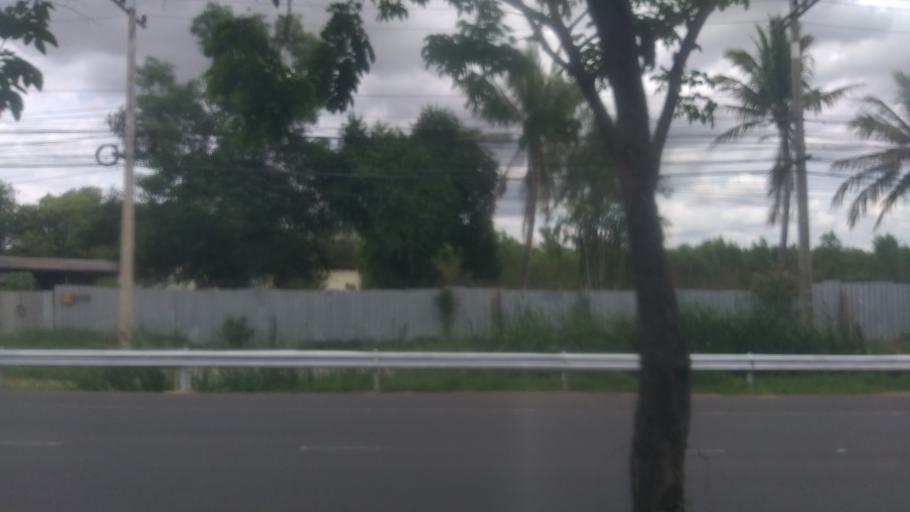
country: TH
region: Nakhon Ratchasima
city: Nakhon Ratchasima
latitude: 15.0485
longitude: 102.1302
